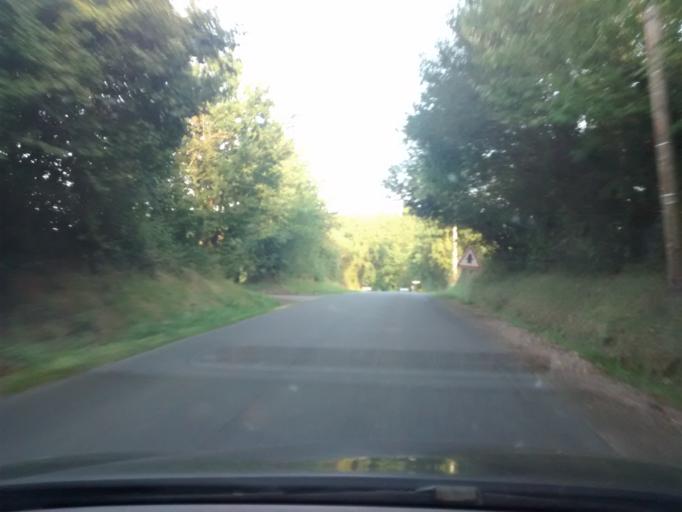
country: FR
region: Lower Normandy
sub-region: Departement du Calvados
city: Villers-sur-Mer
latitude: 49.3176
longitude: 0.0147
